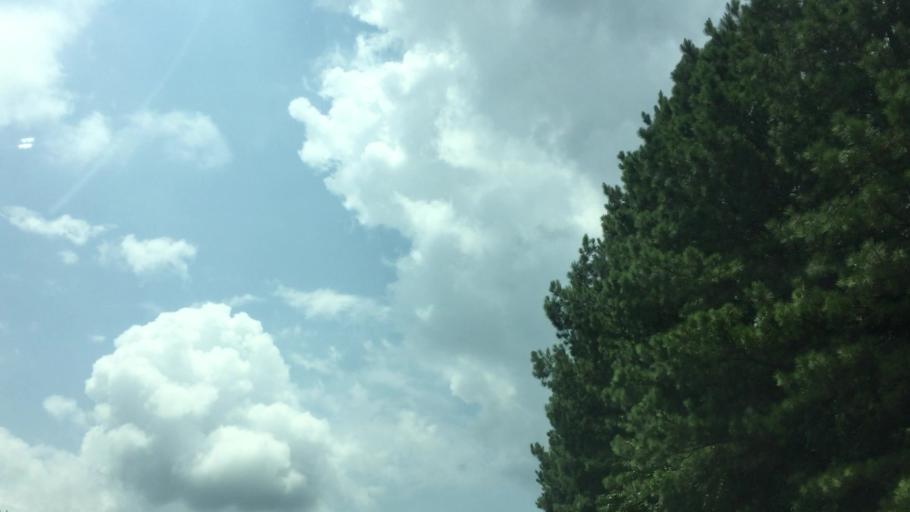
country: US
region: Georgia
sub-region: Fulton County
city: Fairburn
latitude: 33.5873
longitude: -84.6478
